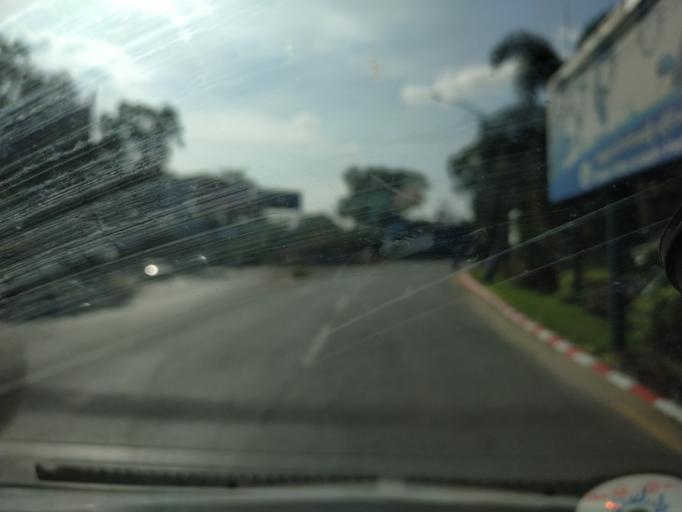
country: MM
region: Ayeyarwady
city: Pathein
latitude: 16.8009
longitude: 94.7622
